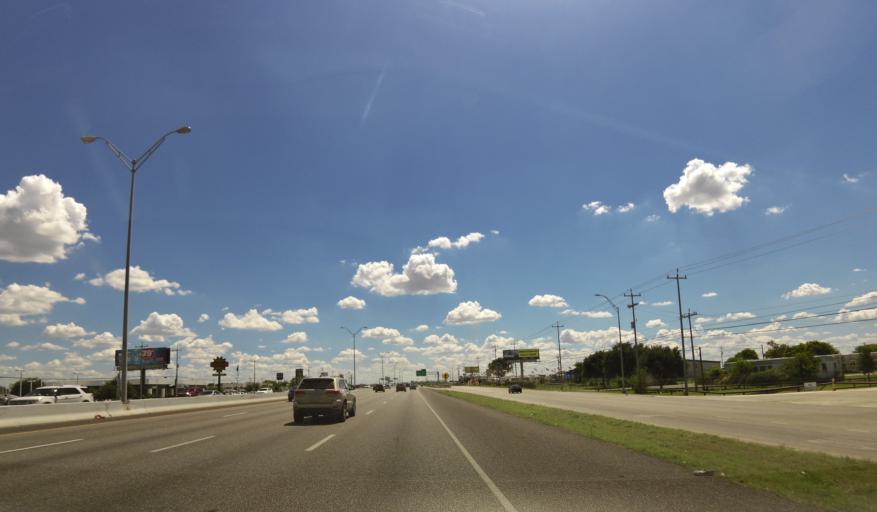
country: US
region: Texas
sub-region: Bexar County
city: Selma
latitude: 29.5901
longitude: -98.2963
